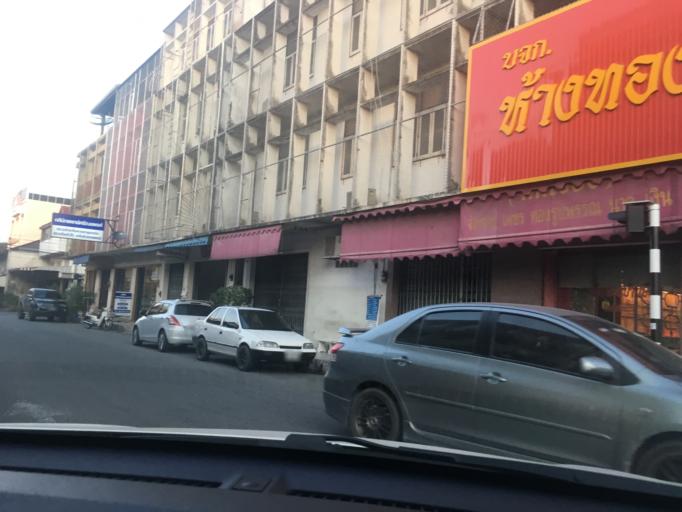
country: TH
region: Chon Buri
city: Ban Bueng
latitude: 13.3102
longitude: 101.1156
